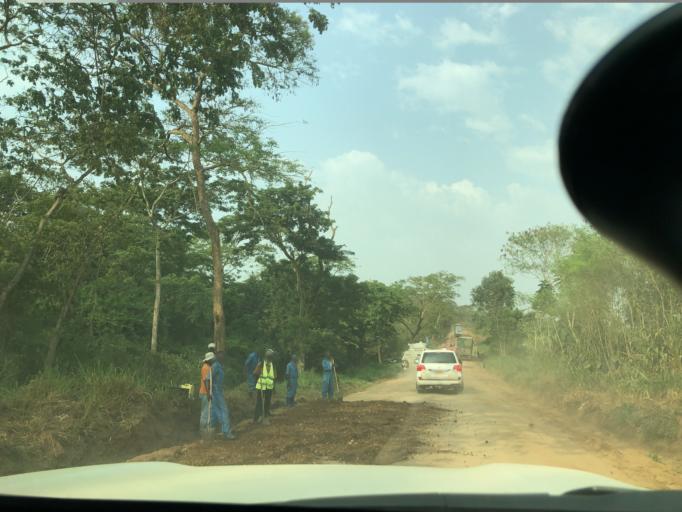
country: UG
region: Western Region
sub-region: Kasese District
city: Margherita
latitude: 0.1946
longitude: 29.6582
